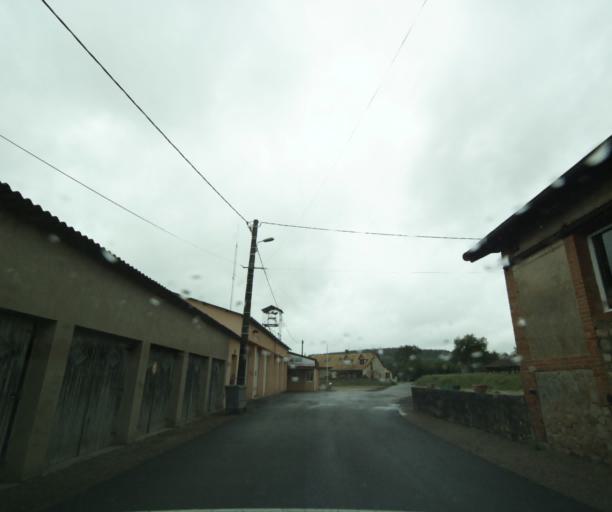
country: FR
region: Bourgogne
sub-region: Departement de Saone-et-Loire
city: Charolles
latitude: 46.4818
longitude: 4.4359
